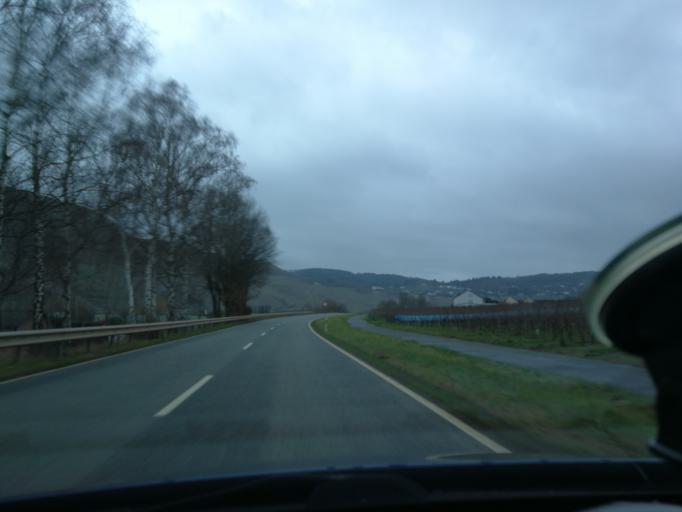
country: DE
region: Rheinland-Pfalz
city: Trittenheim
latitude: 49.8311
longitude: 6.8985
